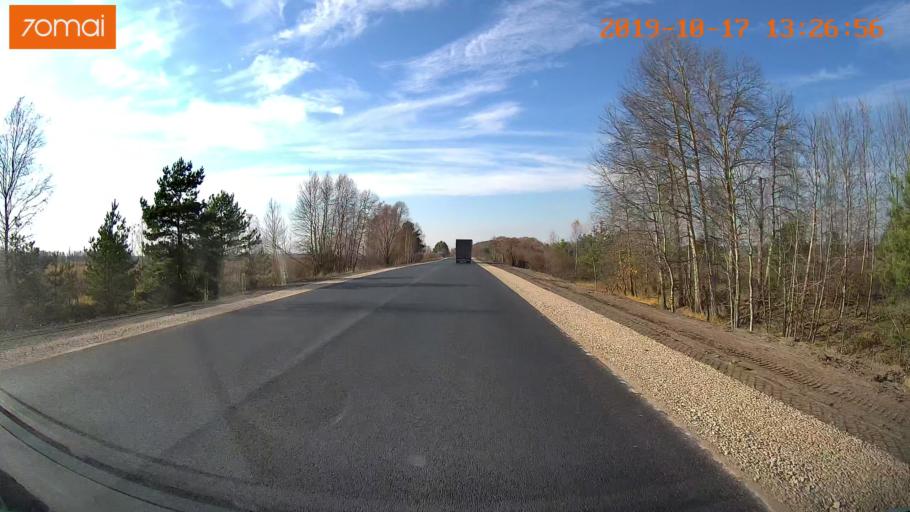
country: RU
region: Rjazan
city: Gus'-Zheleznyy
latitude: 55.1117
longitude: 40.9074
